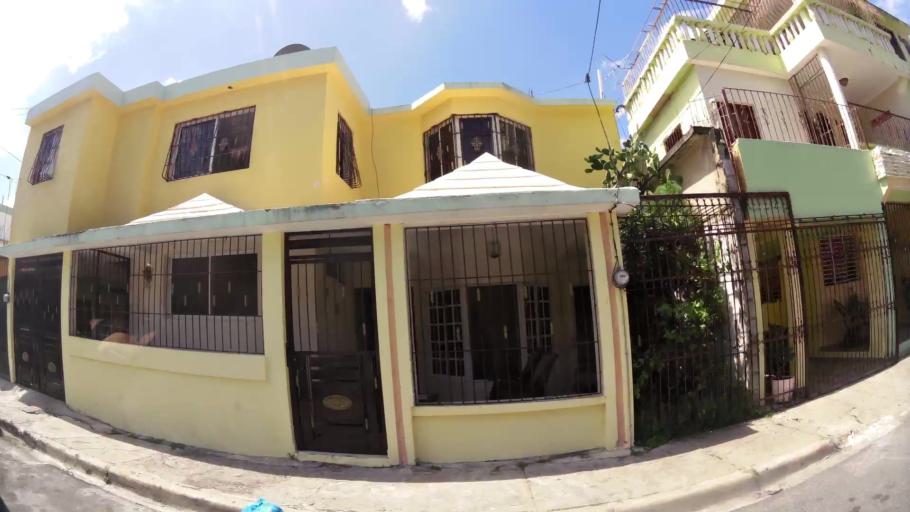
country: DO
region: San Cristobal
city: San Cristobal
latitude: 18.4109
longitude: -70.1086
